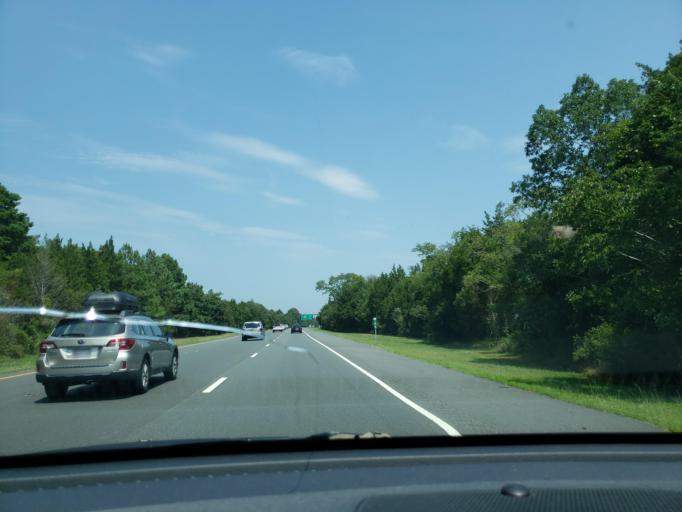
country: US
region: New Jersey
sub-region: Cape May County
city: Sea Isle City
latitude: 39.1836
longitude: -74.7202
